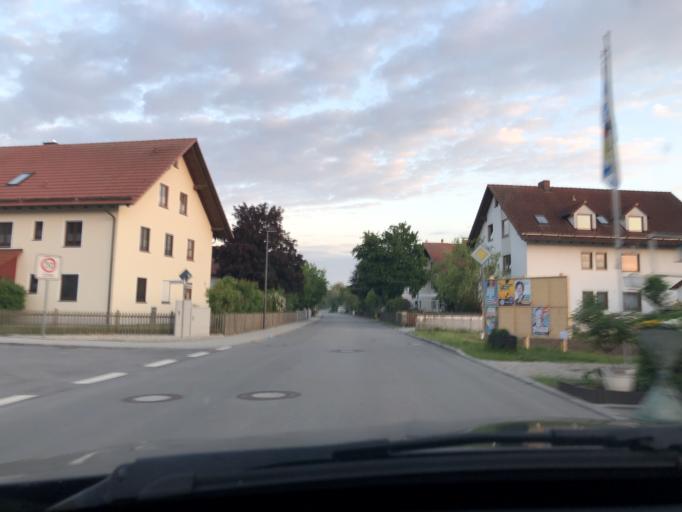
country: DE
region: Bavaria
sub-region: Upper Bavaria
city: Wolfersdorf
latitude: 48.4580
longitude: 11.7074
